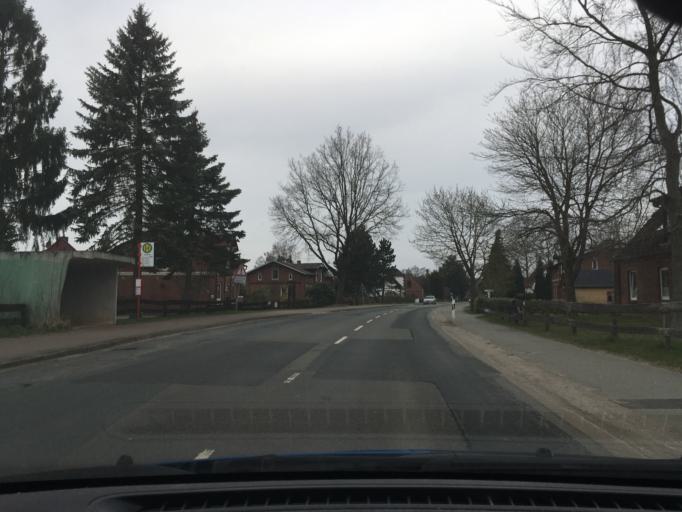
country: DE
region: Lower Saxony
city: Tespe
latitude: 53.3932
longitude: 10.4118
